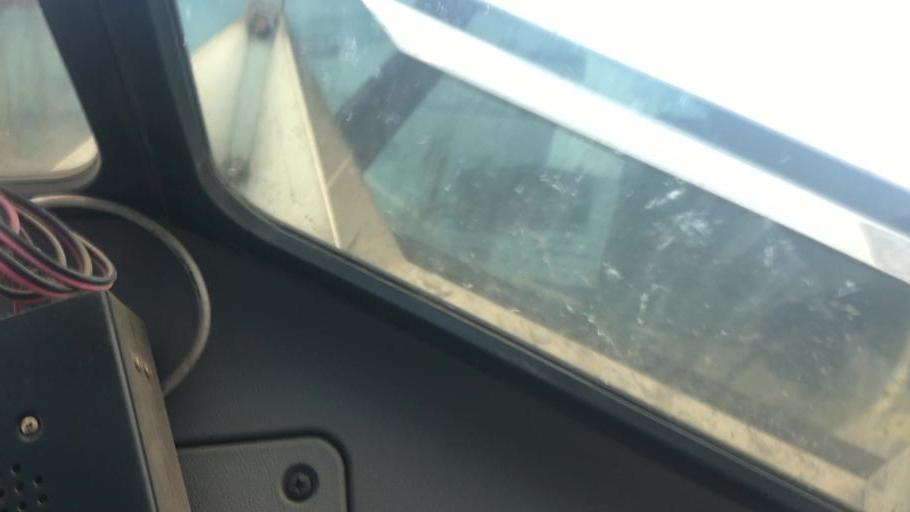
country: US
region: Wisconsin
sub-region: Brown County
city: Allouez
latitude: 44.4897
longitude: -88.0334
